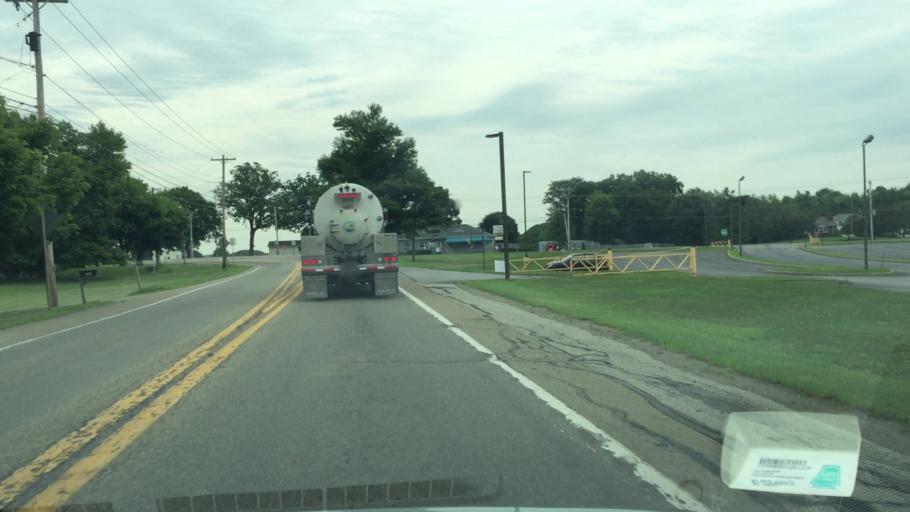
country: US
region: Pennsylvania
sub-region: Butler County
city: Mars
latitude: 40.6929
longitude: -79.9793
